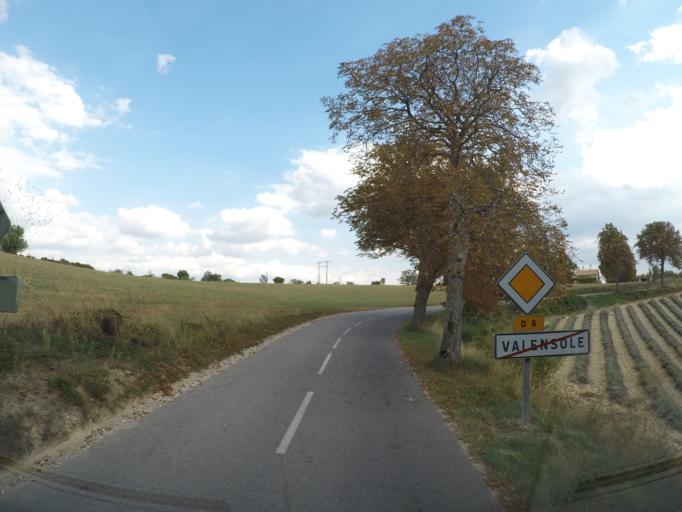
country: FR
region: Provence-Alpes-Cote d'Azur
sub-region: Departement des Alpes-de-Haute-Provence
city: Valensole
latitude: 43.8327
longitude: 5.9916
